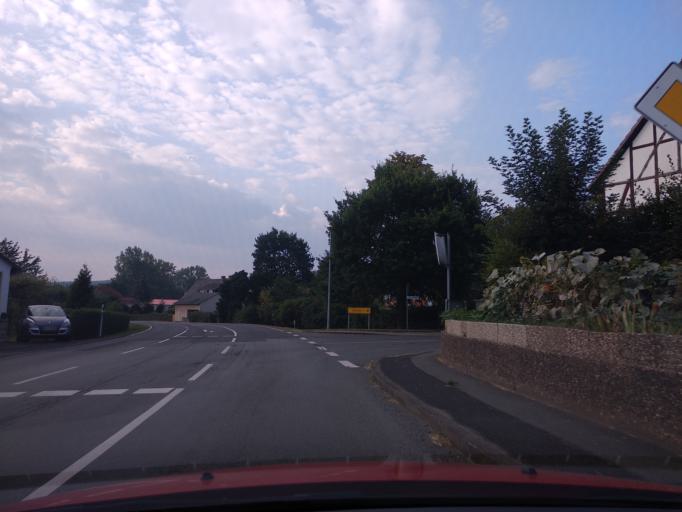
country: DE
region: Hesse
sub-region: Regierungsbezirk Kassel
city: Calden
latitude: 51.3946
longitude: 9.3502
